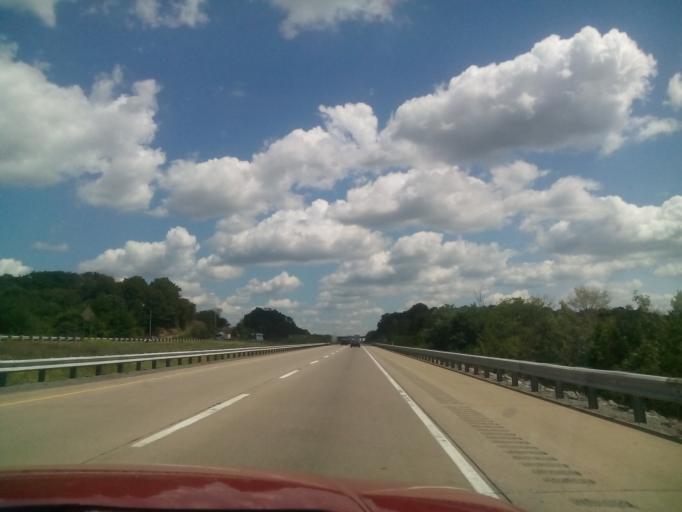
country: US
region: Pennsylvania
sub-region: Northumberland County
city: Riverside
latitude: 40.9860
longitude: -76.7152
